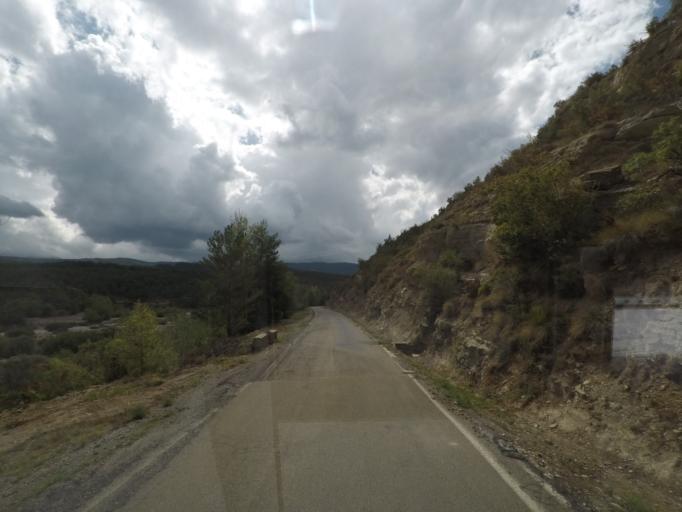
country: ES
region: Aragon
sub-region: Provincia de Huesca
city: Yebra de Basa
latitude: 42.3938
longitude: -0.2699
